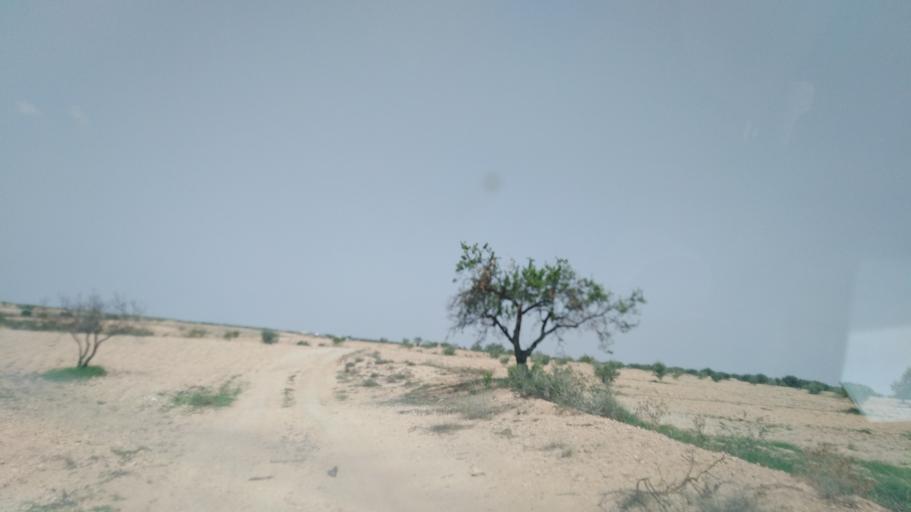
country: TN
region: Safaqis
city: Sfax
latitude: 34.6483
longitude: 10.5579
